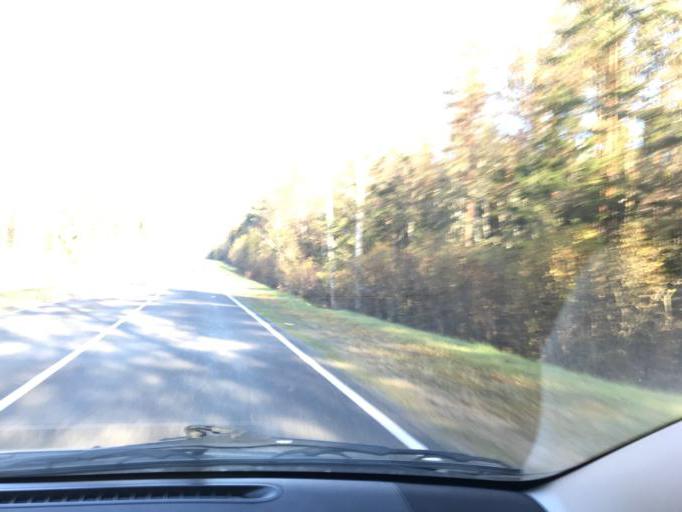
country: BY
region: Vitebsk
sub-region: Ushatski Rayon
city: Ushachy
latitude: 55.0934
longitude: 28.7570
